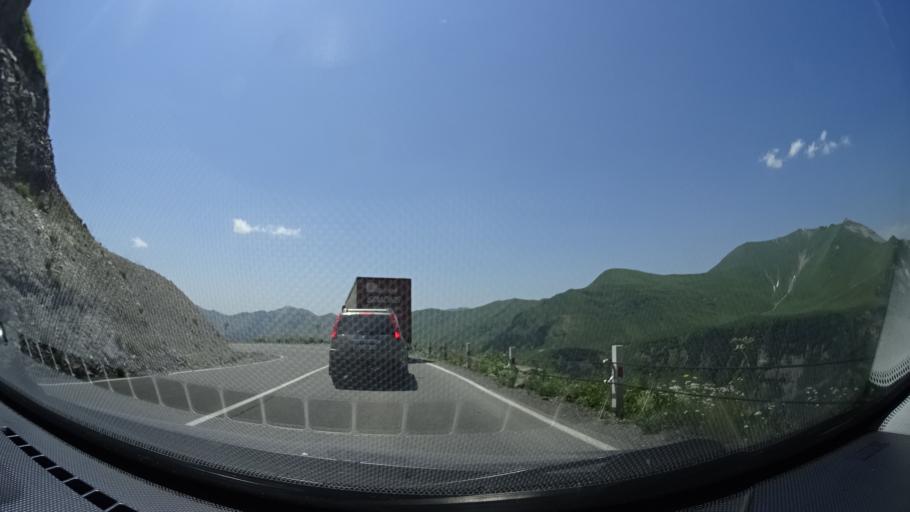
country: GE
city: Gudauri
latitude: 42.4809
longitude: 44.4725
